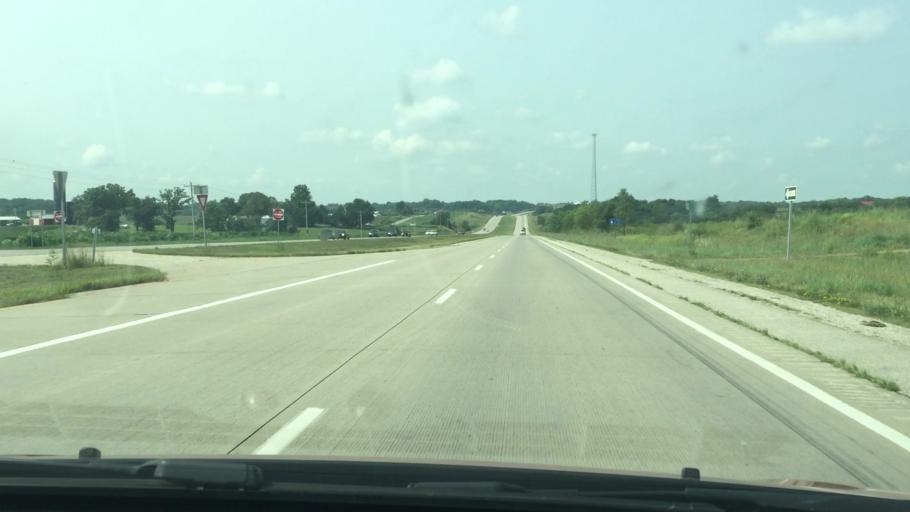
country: US
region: Iowa
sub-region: Cedar County
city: Durant
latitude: 41.5115
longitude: -90.9172
